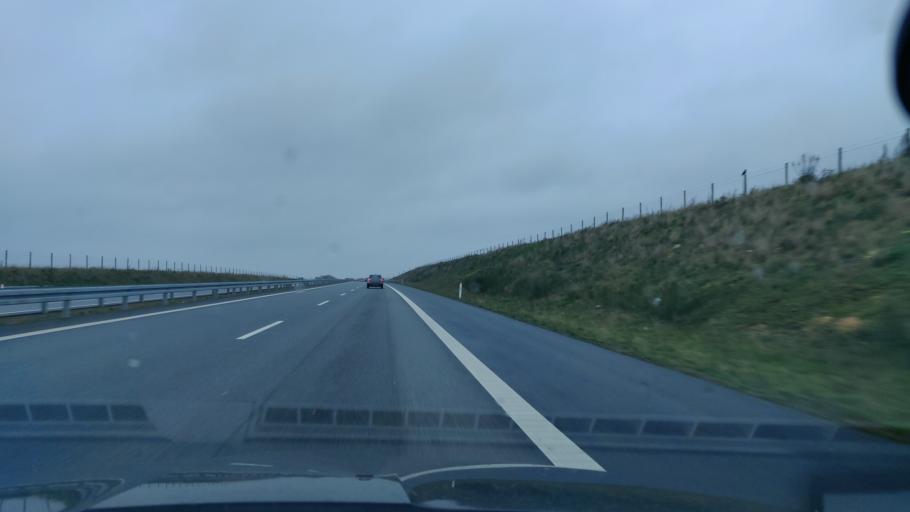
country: DK
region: Central Jutland
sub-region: Herning Kommune
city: Avlum
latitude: 56.2446
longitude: 8.7993
